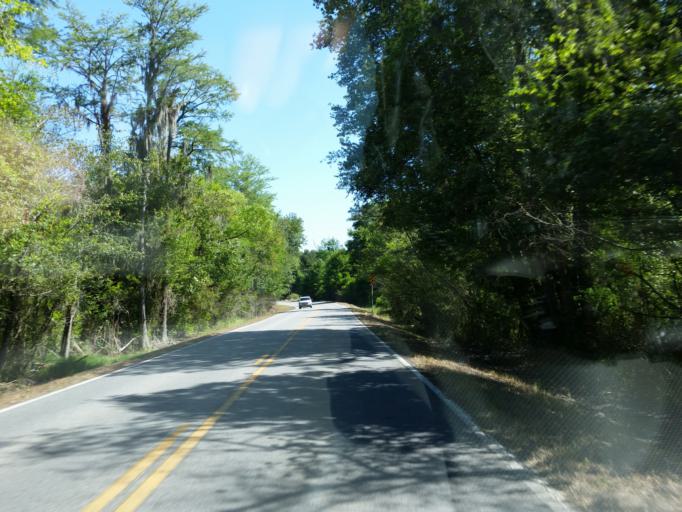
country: US
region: Georgia
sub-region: Cook County
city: Adel
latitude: 31.1103
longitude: -83.4140
